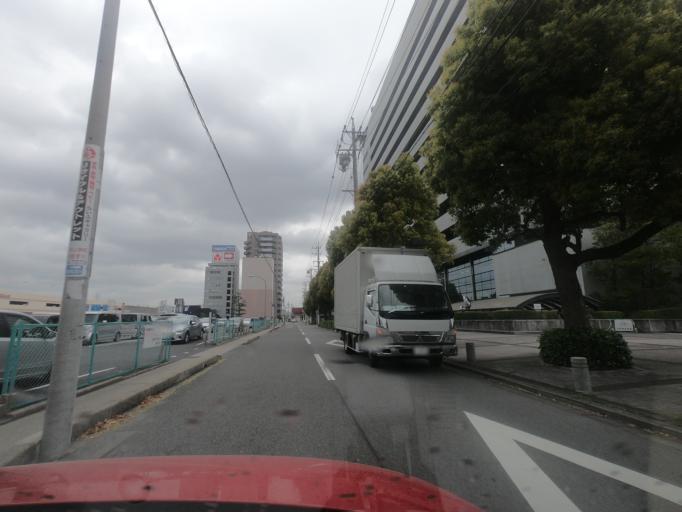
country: JP
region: Aichi
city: Kasugai
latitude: 35.2476
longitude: 136.9714
